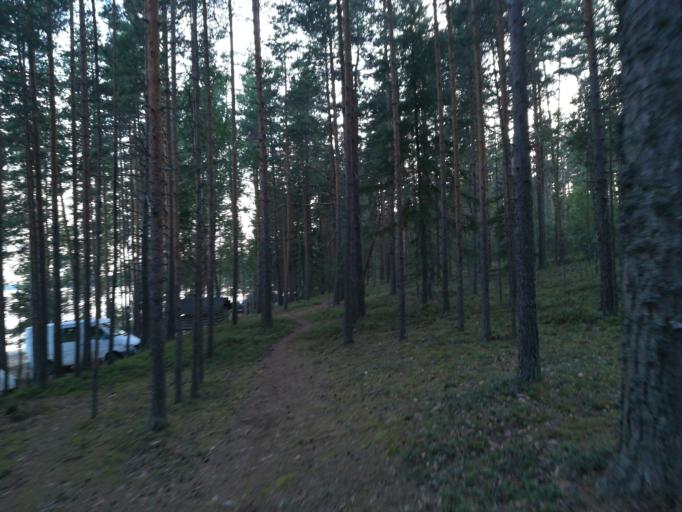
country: FI
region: South Karelia
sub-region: Lappeenranta
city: Joutseno
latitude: 61.3357
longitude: 28.3993
